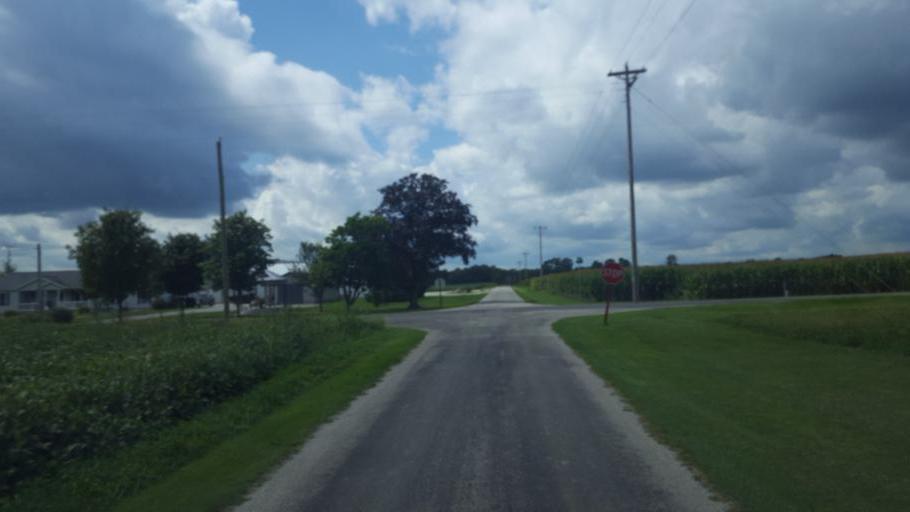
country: US
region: Ohio
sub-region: Huron County
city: Plymouth
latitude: 41.0782
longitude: -82.6420
